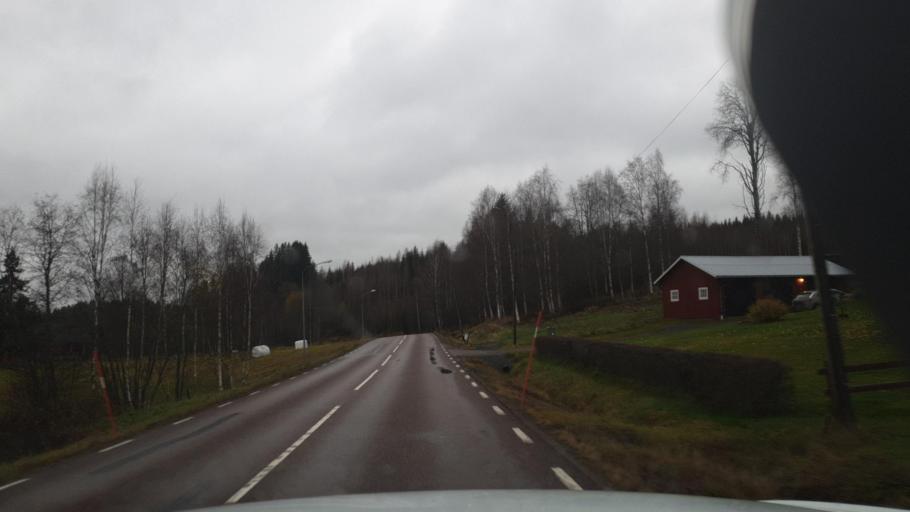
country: SE
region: Vaermland
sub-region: Eda Kommun
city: Amotfors
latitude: 59.8573
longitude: 12.5495
